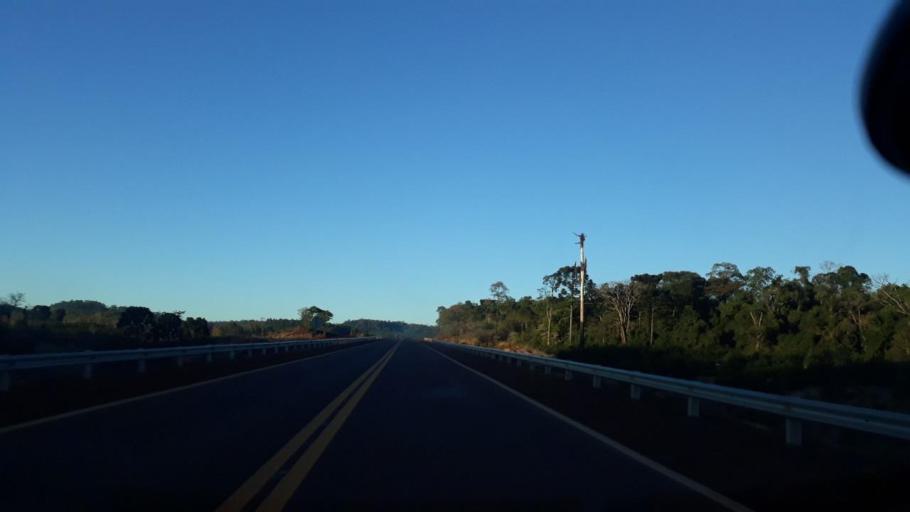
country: AR
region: Misiones
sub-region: Departamento de San Pedro
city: San Pedro
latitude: -26.5418
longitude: -53.9598
